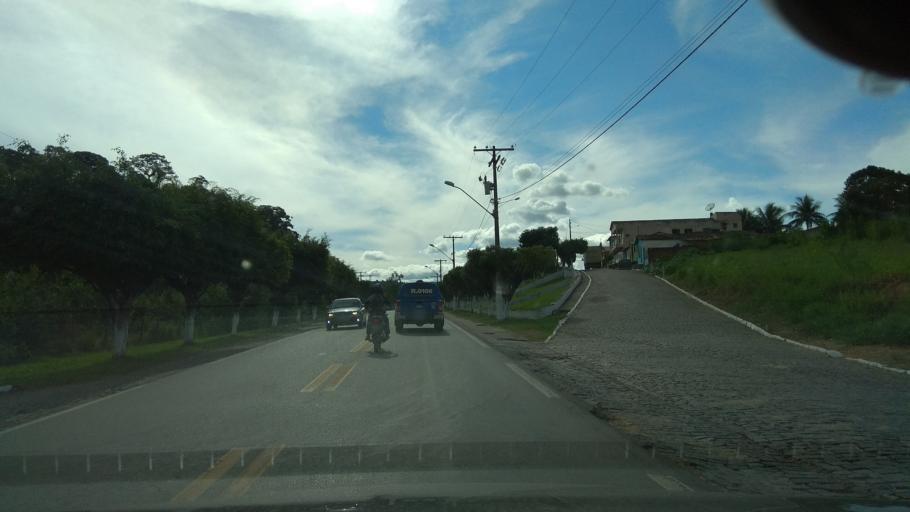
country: BR
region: Bahia
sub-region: Jitauna
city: Jitauna
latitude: -14.0155
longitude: -39.8905
